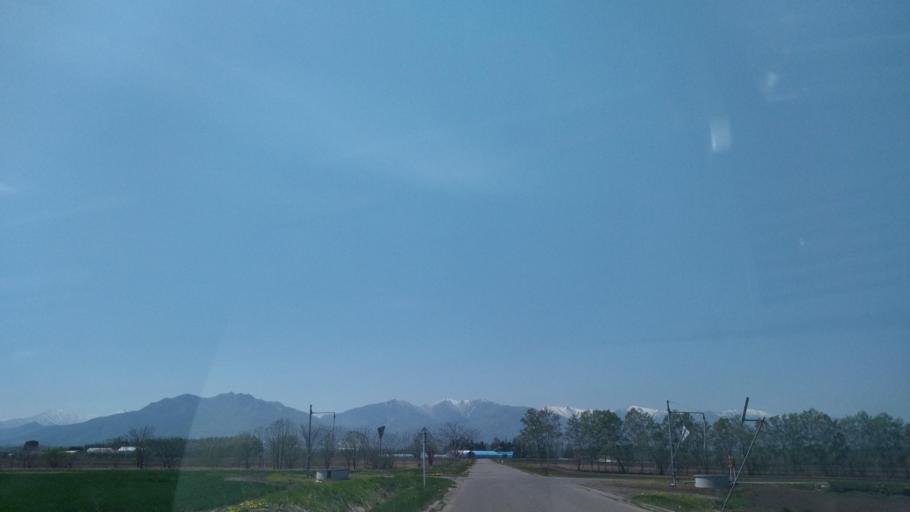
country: JP
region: Hokkaido
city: Obihiro
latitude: 42.8931
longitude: 143.0120
